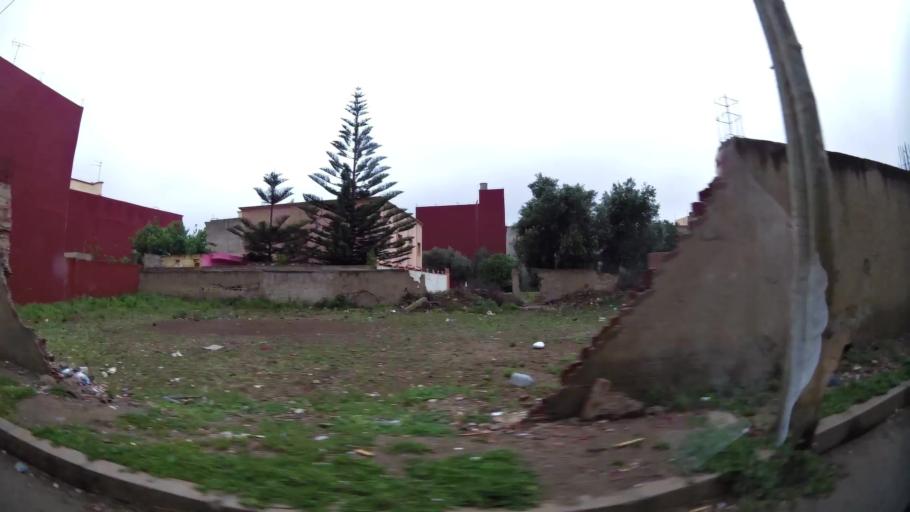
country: MA
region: Oriental
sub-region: Nador
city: Nador
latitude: 35.1601
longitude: -2.9529
